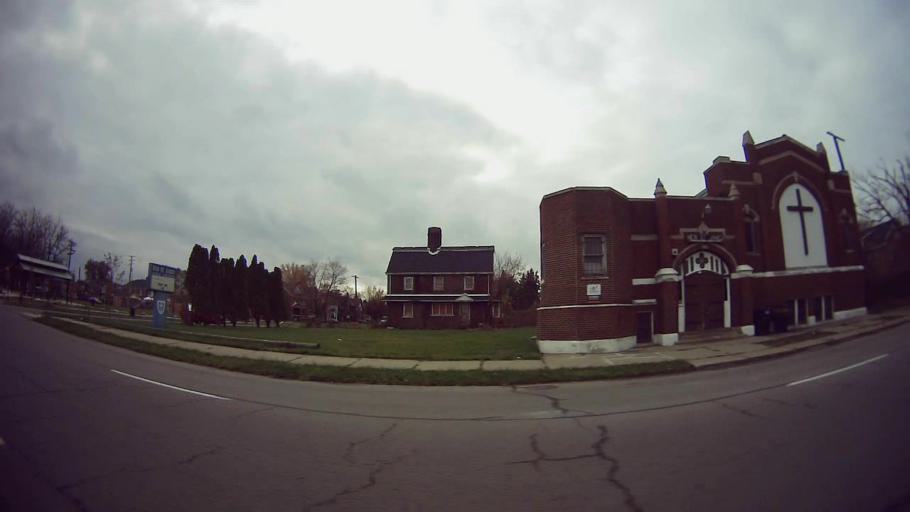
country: US
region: Michigan
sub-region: Wayne County
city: Highland Park
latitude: 42.3775
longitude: -83.1002
